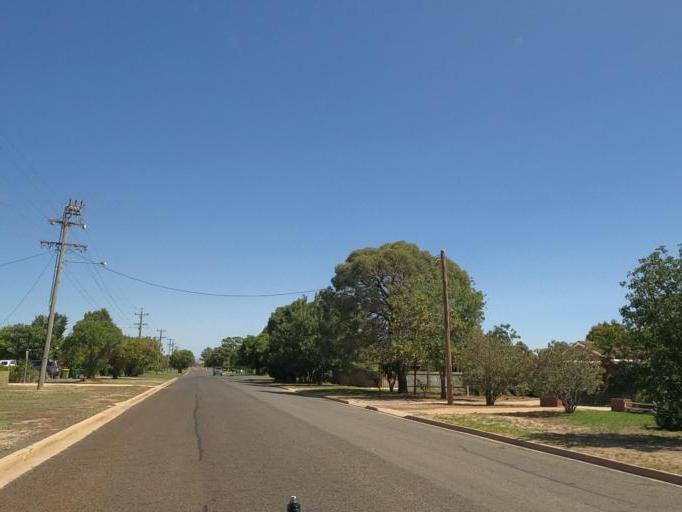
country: AU
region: New South Wales
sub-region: Corowa Shire
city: Mulwala
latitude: -35.9839
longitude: 146.0087
